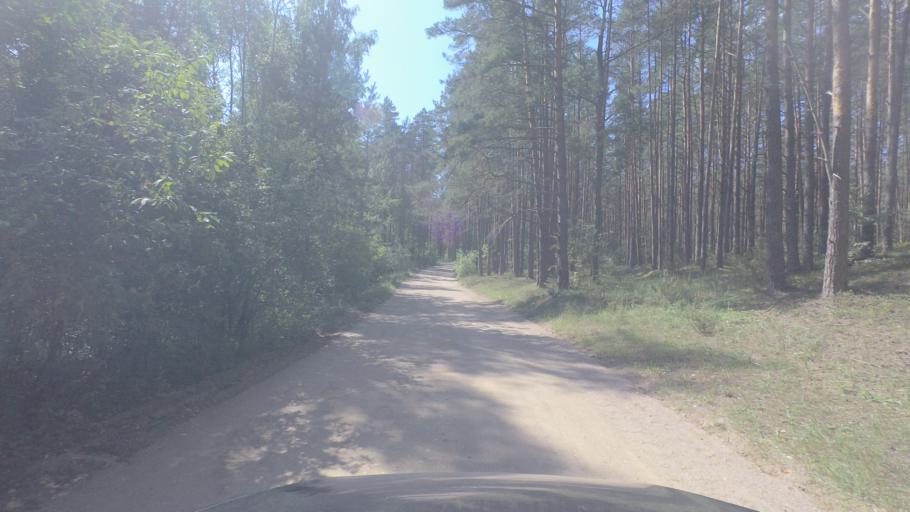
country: LT
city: Nemencine
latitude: 54.8483
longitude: 25.4999
